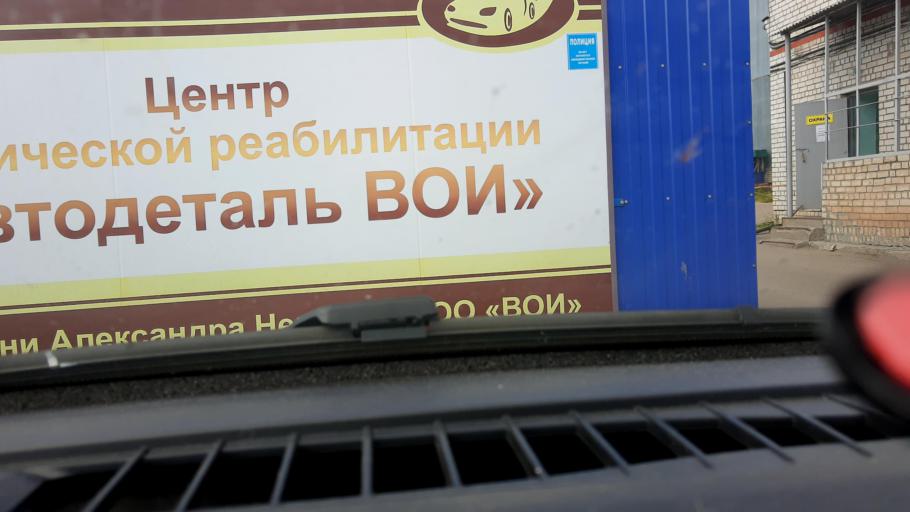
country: RU
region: Nizjnij Novgorod
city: Gorbatovka
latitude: 56.2546
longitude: 43.8797
